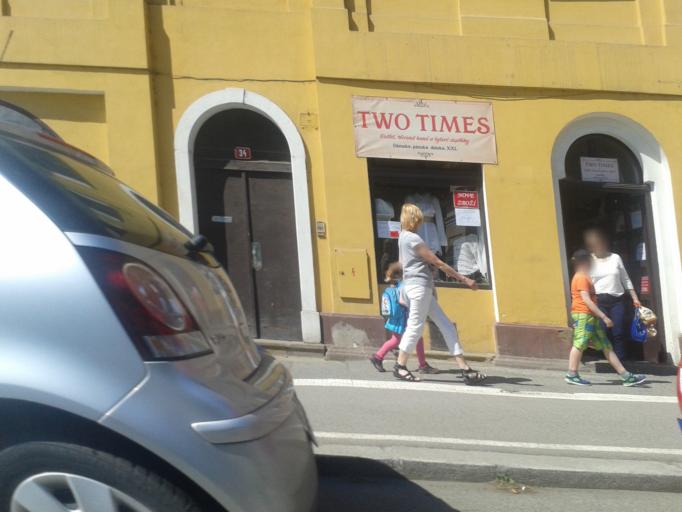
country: CZ
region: Central Bohemia
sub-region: Okres Beroun
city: Beroun
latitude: 49.9616
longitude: 14.0668
